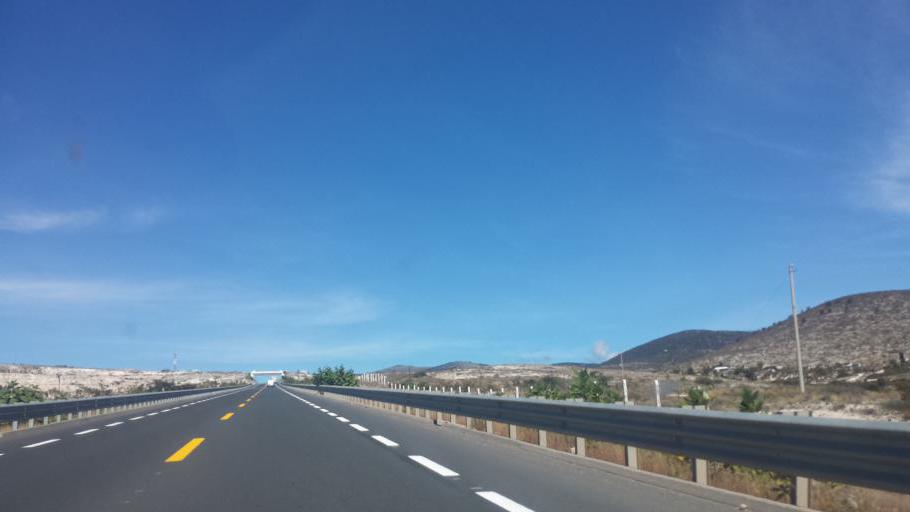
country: MX
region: Oaxaca
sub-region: Villa Tejupam de la Union
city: Villa Tejupam de la Union
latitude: 17.9305
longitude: -97.3577
